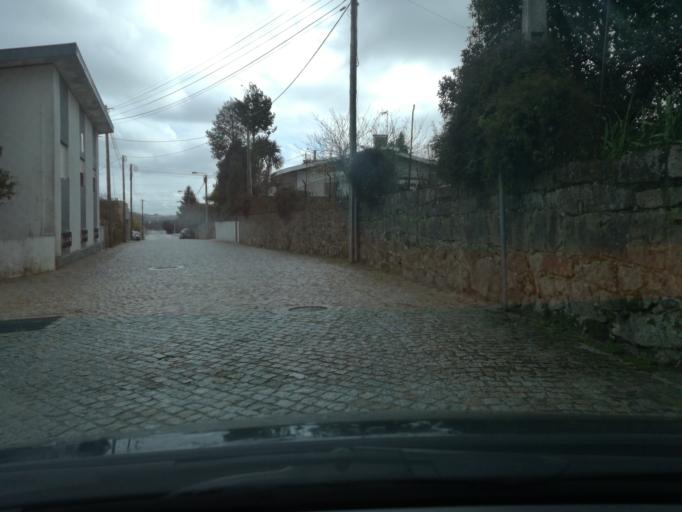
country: PT
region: Porto
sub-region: Valongo
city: Ermesinde
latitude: 41.2408
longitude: -8.5481
